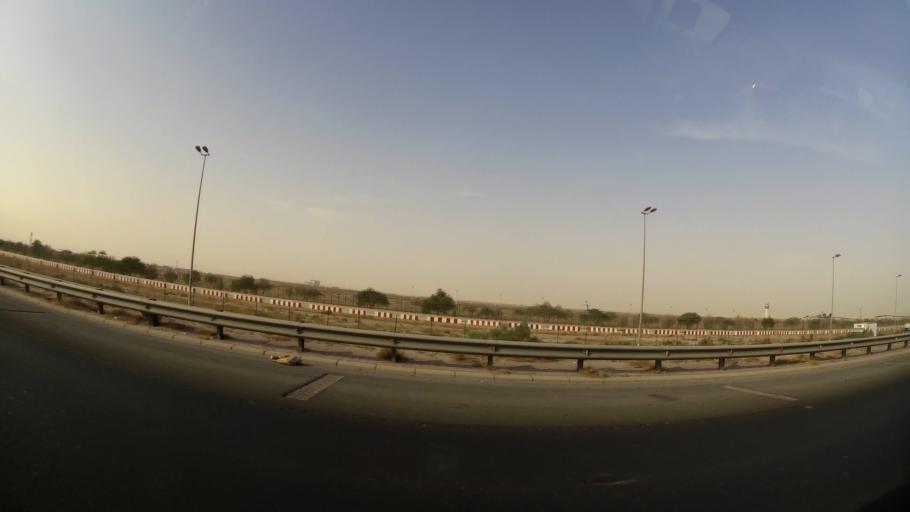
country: KW
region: Al Farwaniyah
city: Janub as Surrah
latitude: 29.2194
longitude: 47.9993
